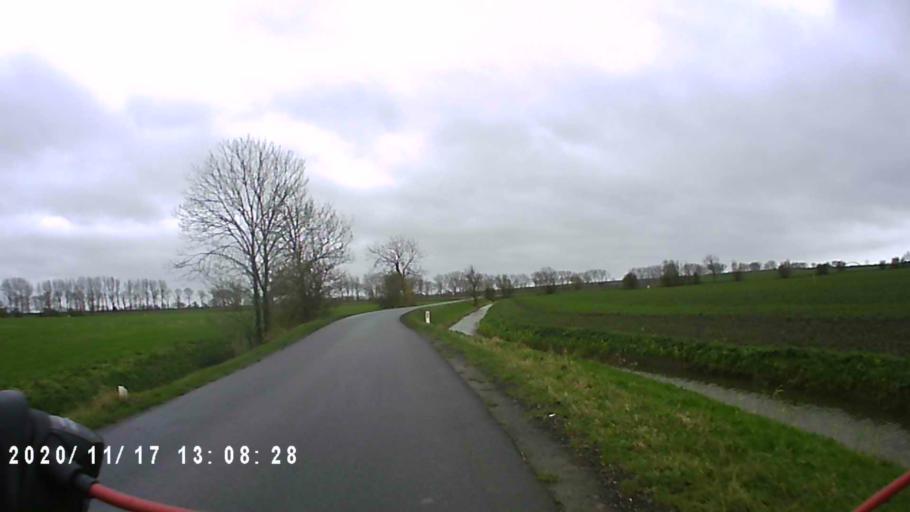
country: NL
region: Groningen
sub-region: Gemeente Zuidhorn
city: Zuidhorn
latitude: 53.2635
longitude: 6.4263
